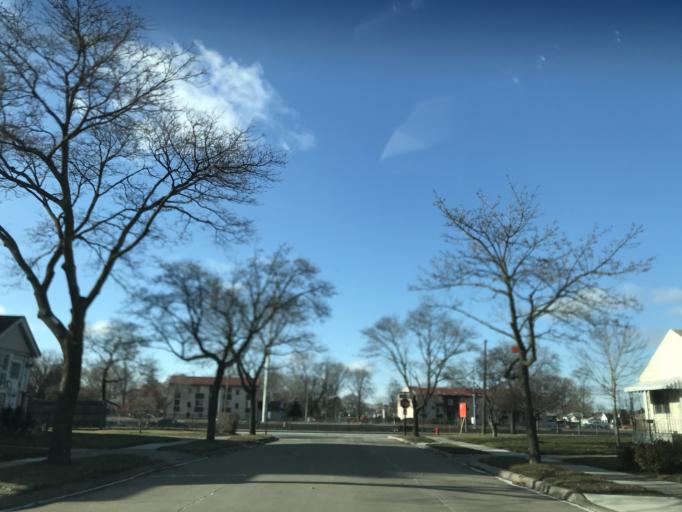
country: US
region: Michigan
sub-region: Oakland County
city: Hazel Park
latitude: 42.4658
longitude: -83.1067
